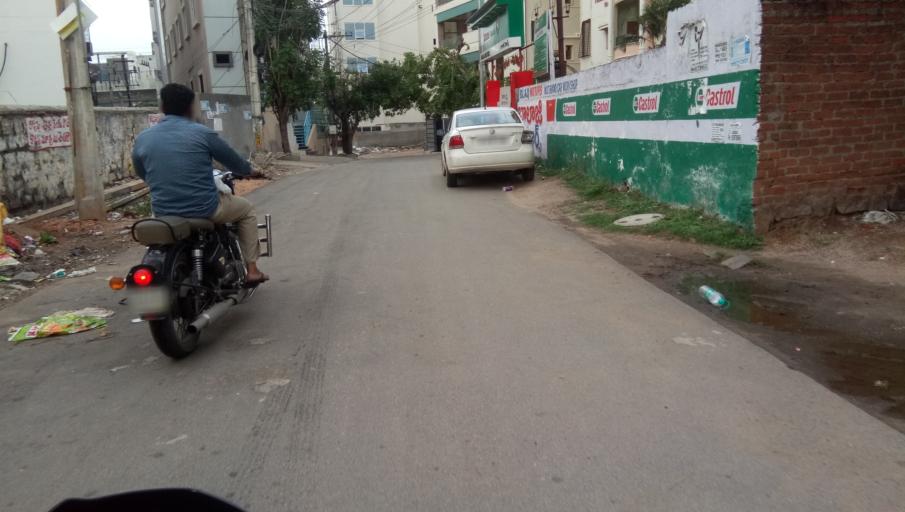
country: IN
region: Telangana
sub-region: Rangareddi
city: Gaddi Annaram
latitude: 17.3601
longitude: 78.5421
